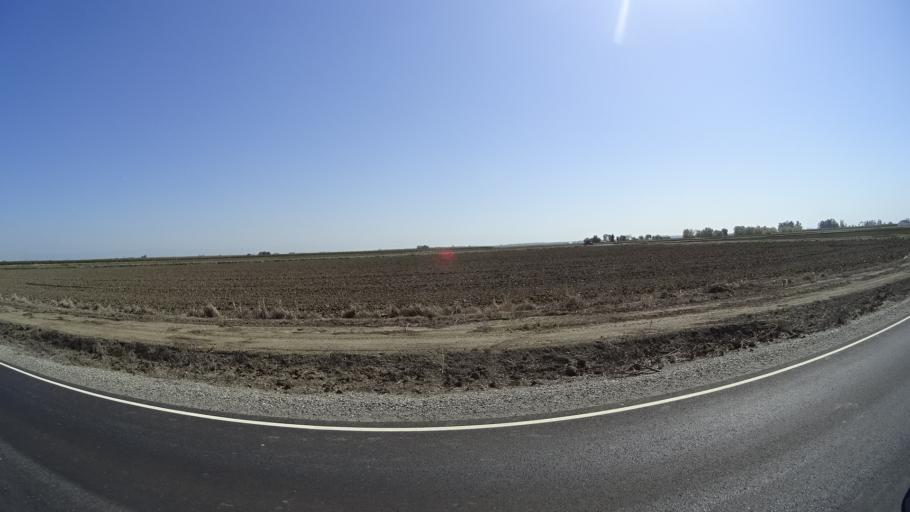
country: US
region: California
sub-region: Glenn County
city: Hamilton City
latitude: 39.6096
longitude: -122.0659
